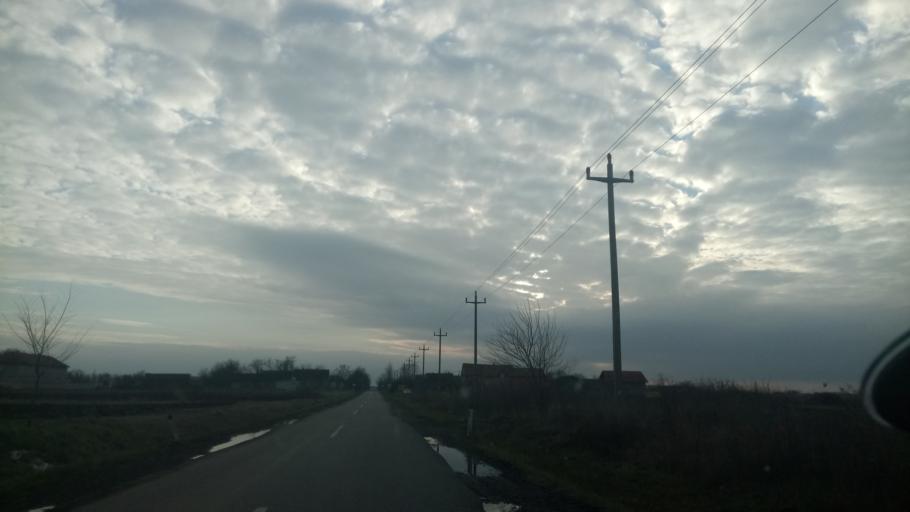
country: RS
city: Vojka
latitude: 44.9446
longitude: 20.1736
